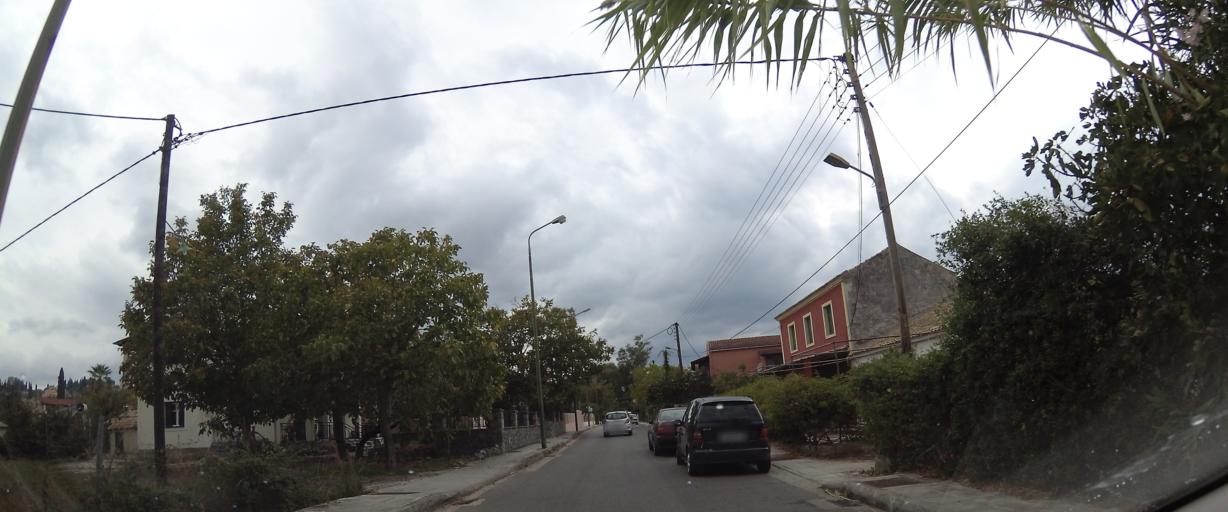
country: GR
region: Ionian Islands
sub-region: Nomos Kerkyras
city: Kontokali
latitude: 39.6462
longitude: 19.8496
